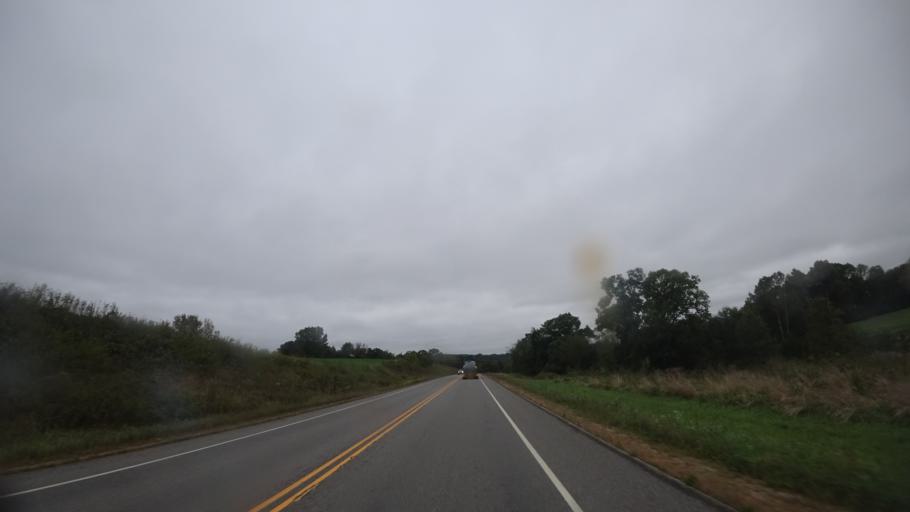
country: US
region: Wisconsin
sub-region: Crawford County
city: Prairie du Chien
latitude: 43.0183
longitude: -91.0336
